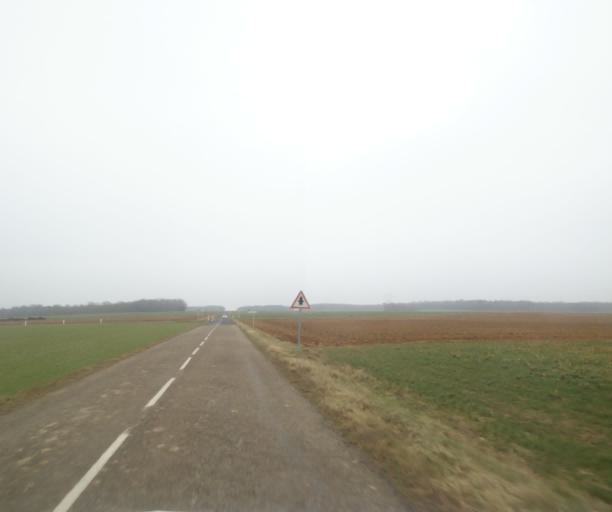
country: FR
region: Champagne-Ardenne
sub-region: Departement de la Haute-Marne
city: Bienville
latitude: 48.5220
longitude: 5.0493
